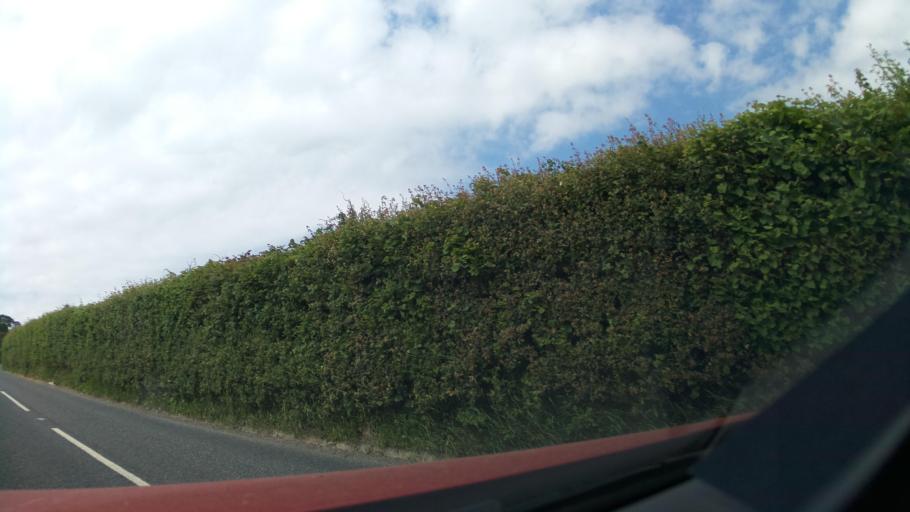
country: GB
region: England
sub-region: Somerset
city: Milborne Port
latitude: 51.0249
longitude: -2.4631
